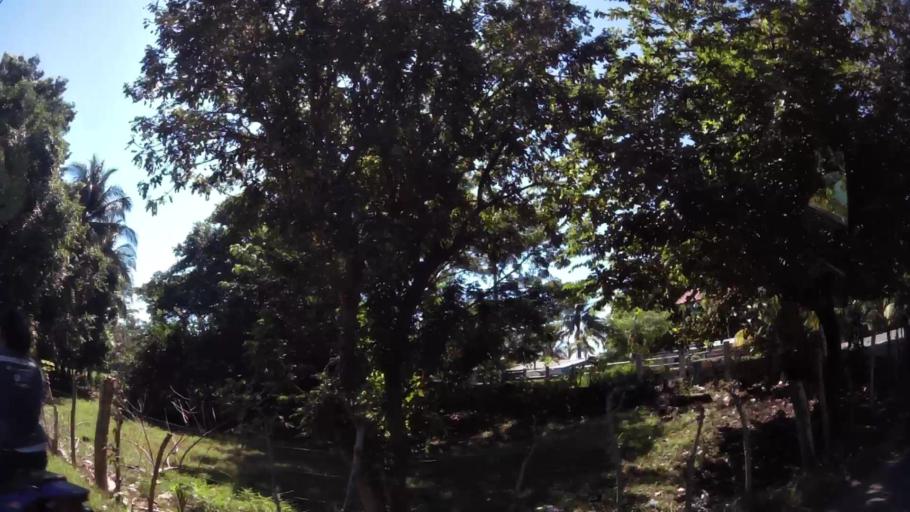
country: GT
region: Escuintla
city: Iztapa
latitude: 13.9399
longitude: -90.7146
